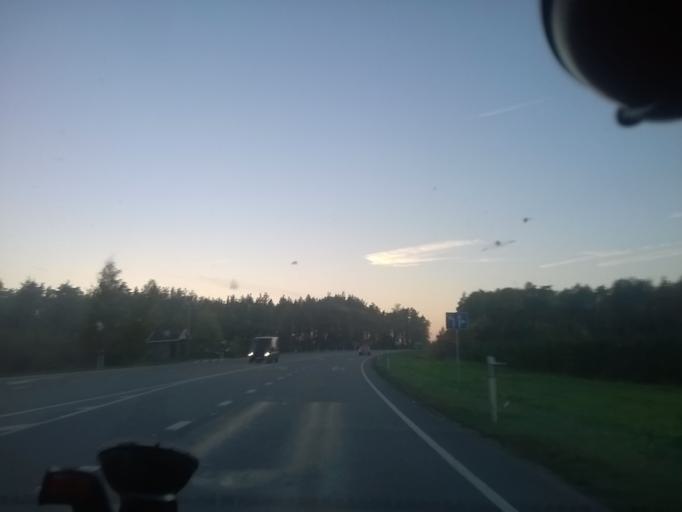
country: EE
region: Laeaene
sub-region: Ridala Parish
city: Uuemoisa
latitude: 58.9566
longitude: 23.7282
